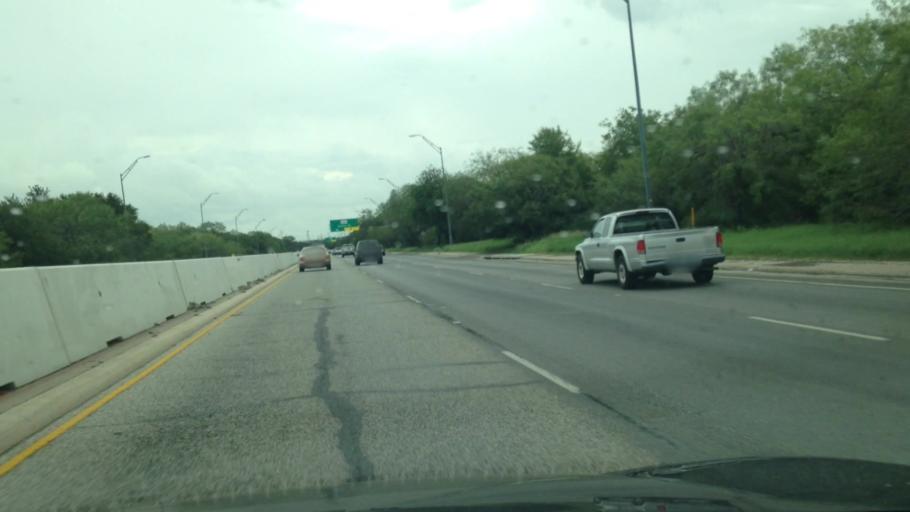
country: US
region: Texas
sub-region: Bexar County
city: Shavano Park
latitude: 29.5596
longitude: -98.5281
